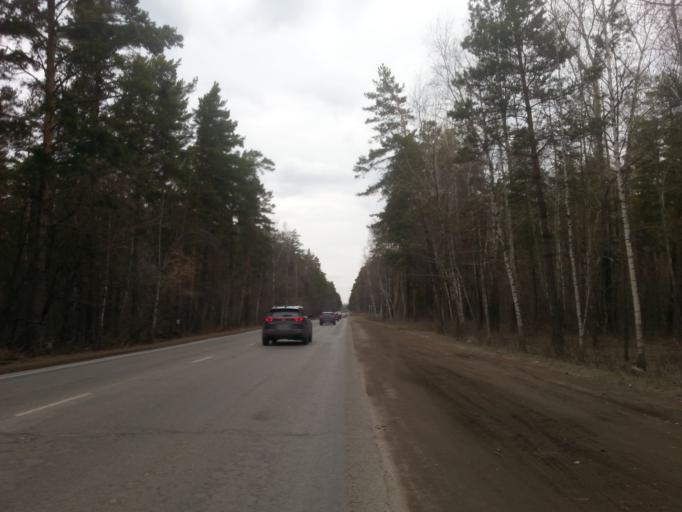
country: RU
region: Altai Krai
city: Yuzhnyy
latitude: 53.2757
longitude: 83.7207
